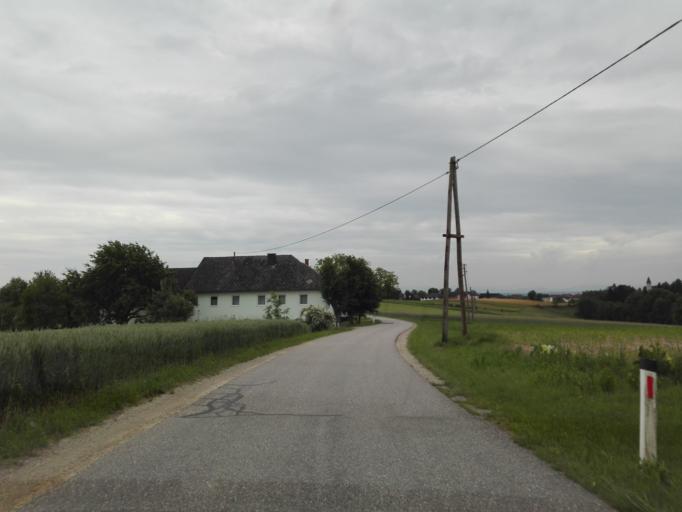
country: AT
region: Upper Austria
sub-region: Politischer Bezirk Perg
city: Perg
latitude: 48.2544
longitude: 14.6799
